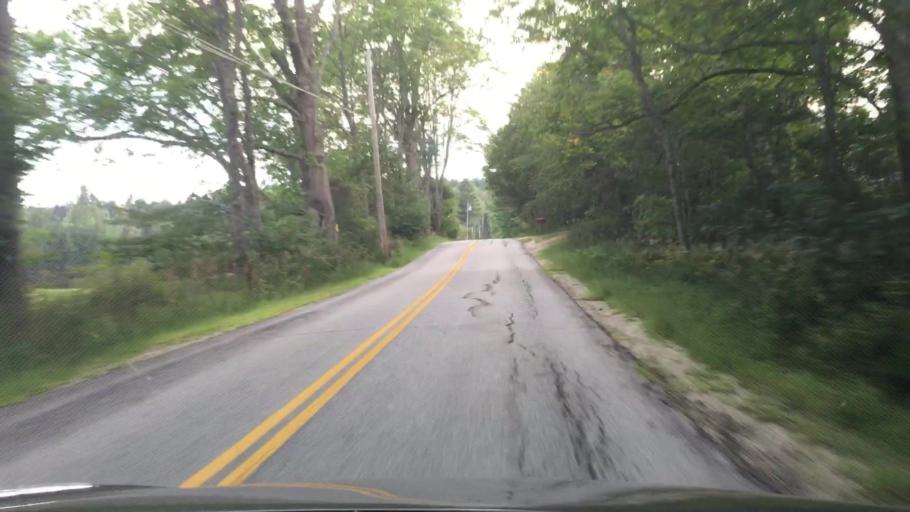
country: US
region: Maine
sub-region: Hancock County
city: Penobscot
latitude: 44.4463
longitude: -68.6214
